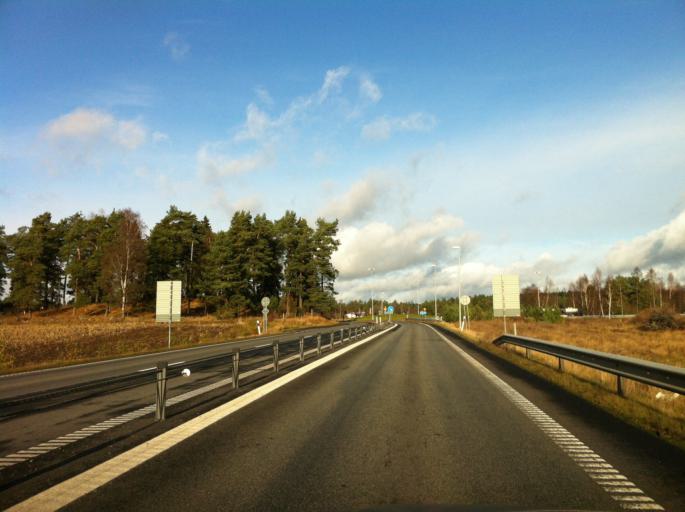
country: SE
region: Skane
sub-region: Osby Kommun
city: Osby
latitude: 56.3876
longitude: 14.0375
